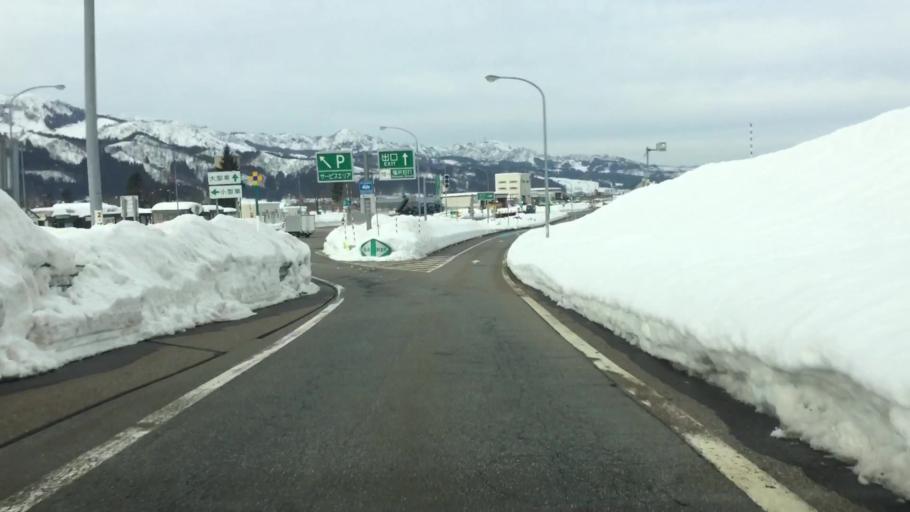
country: JP
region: Niigata
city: Shiozawa
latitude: 36.9953
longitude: 138.8190
